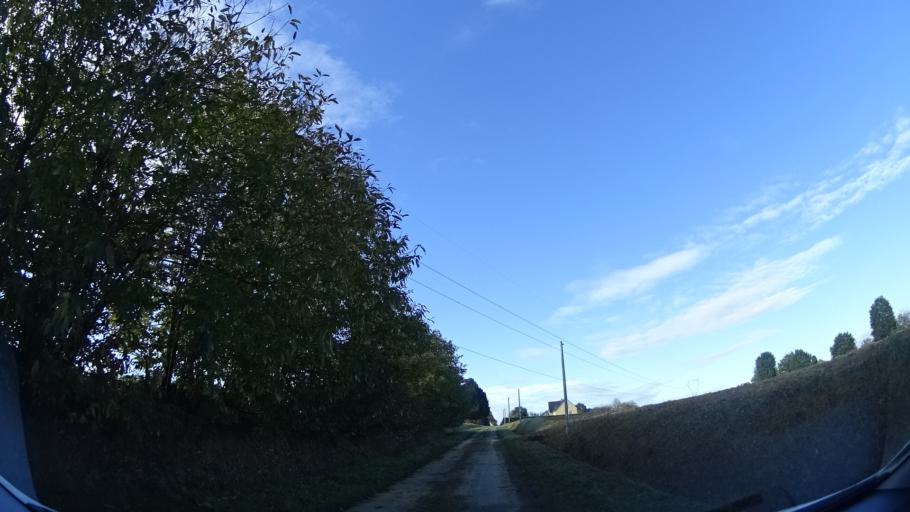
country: FR
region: Brittany
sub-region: Departement d'Ille-et-Vilaine
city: Geveze
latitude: 48.1978
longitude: -1.7883
